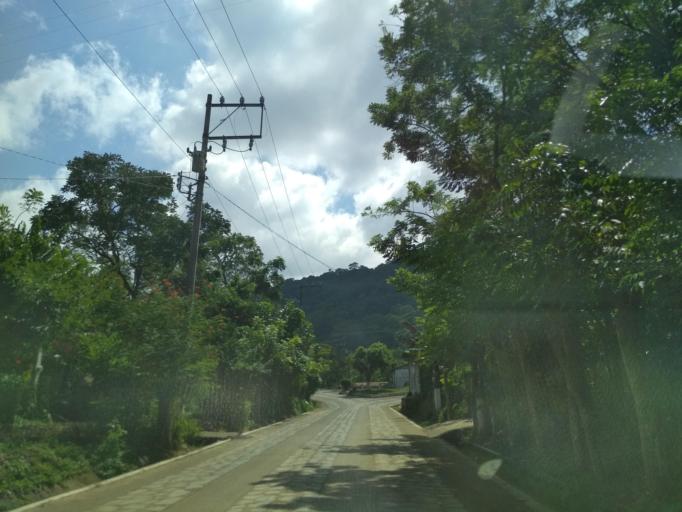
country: MX
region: Veracruz
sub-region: San Andres Tuxtla
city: Texcaltitan Xoteapan (Texcaltitan)
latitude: 18.4443
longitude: -95.2515
